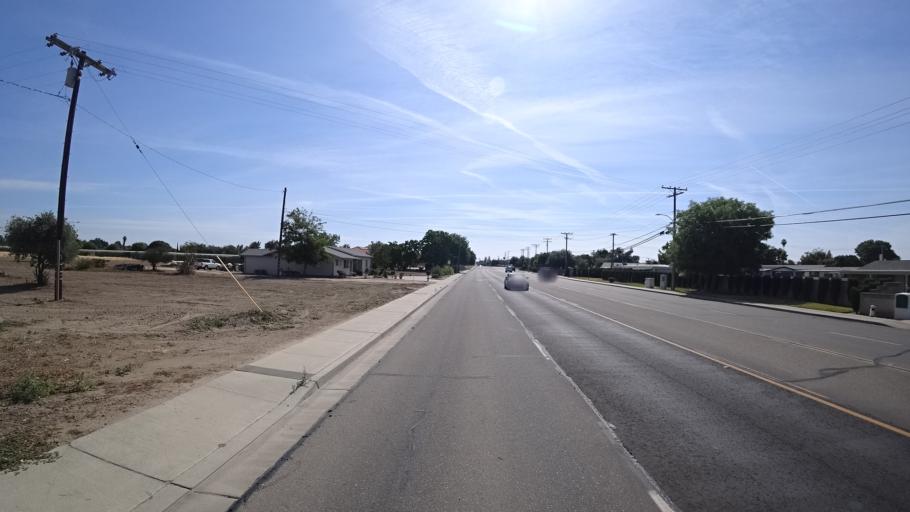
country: US
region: California
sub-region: Kings County
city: Hanford
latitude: 36.3427
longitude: -119.6650
